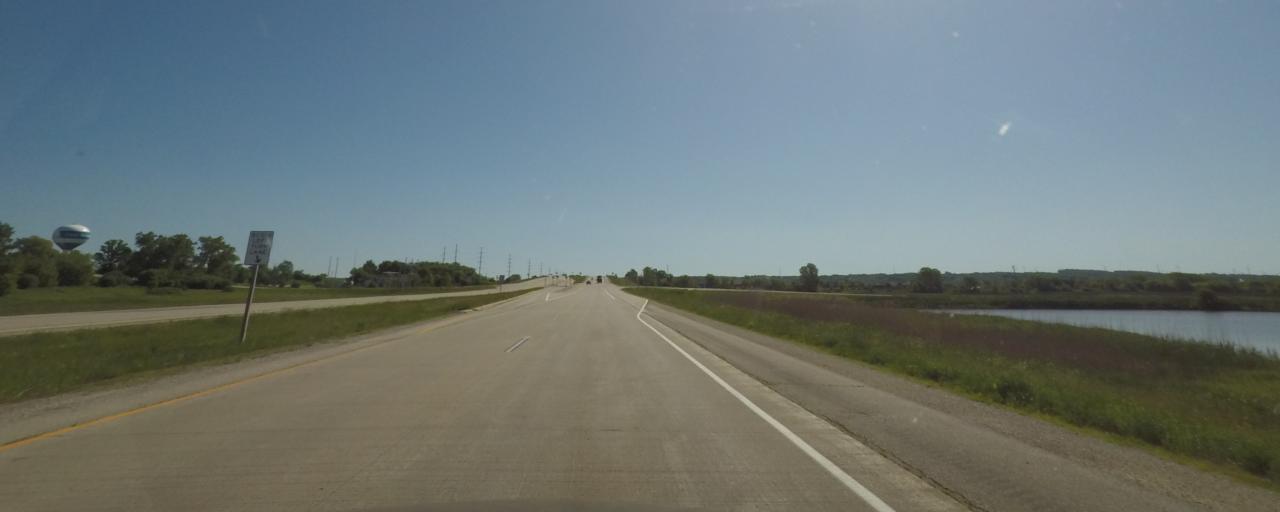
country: US
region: Wisconsin
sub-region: Fond du Lac County
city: Fond du Lac
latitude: 43.7380
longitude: -88.4347
